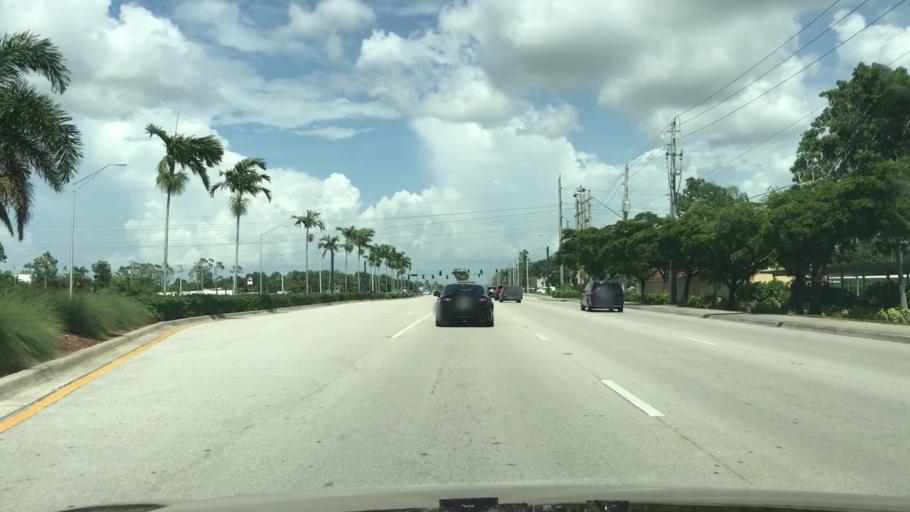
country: US
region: Florida
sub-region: Collier County
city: Naples Park
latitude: 26.2726
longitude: -81.7566
